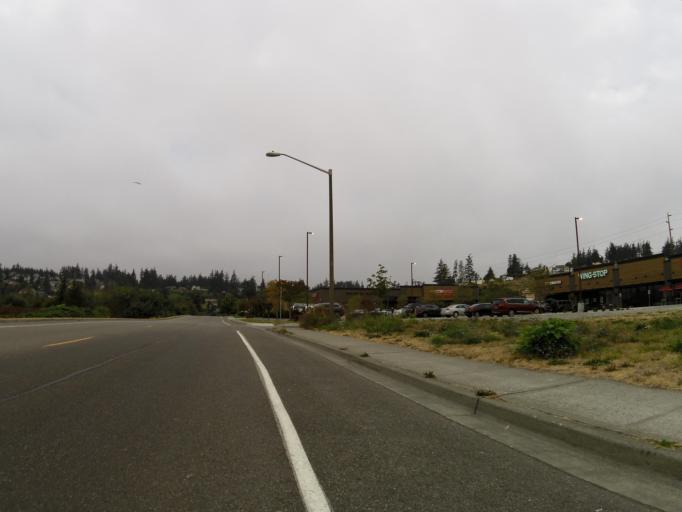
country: US
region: Washington
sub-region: Island County
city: Oak Harbor
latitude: 48.2855
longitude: -122.6593
